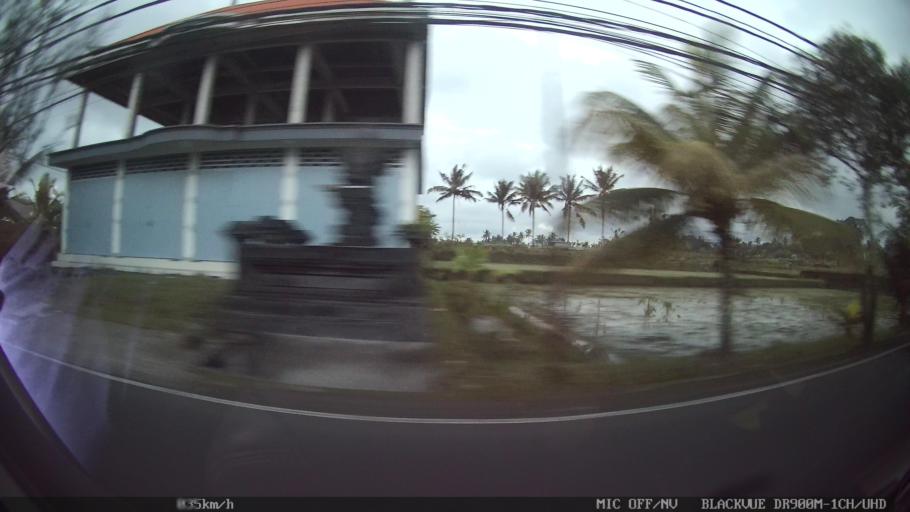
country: ID
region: Bali
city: Bayad
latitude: -8.4535
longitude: 115.2432
